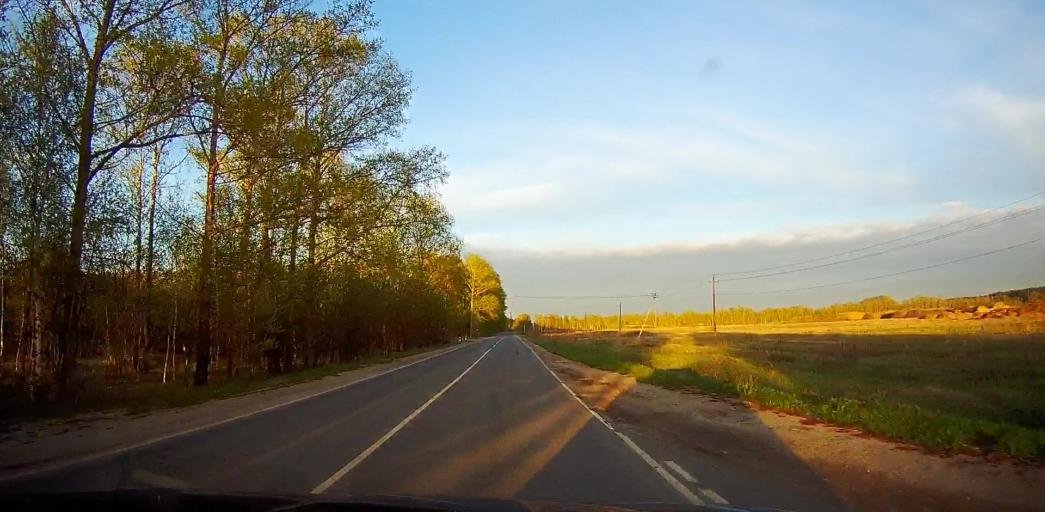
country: RU
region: Moskovskaya
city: Peski
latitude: 55.2100
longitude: 38.6997
